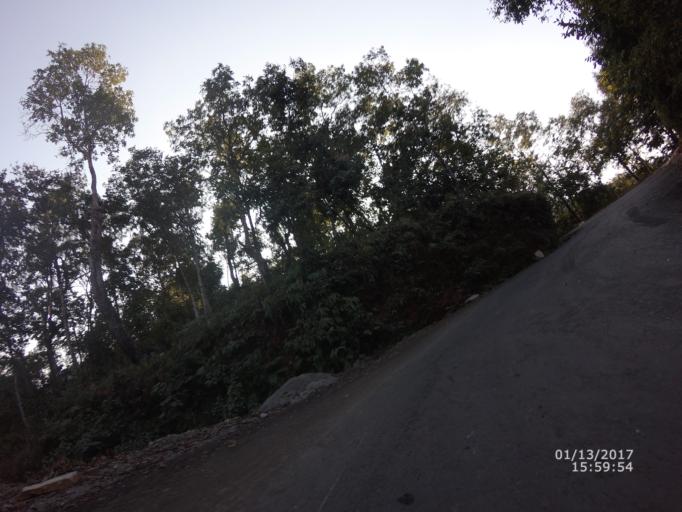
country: NP
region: Western Region
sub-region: Gandaki Zone
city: Pokhara
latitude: 28.1575
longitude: 83.9991
